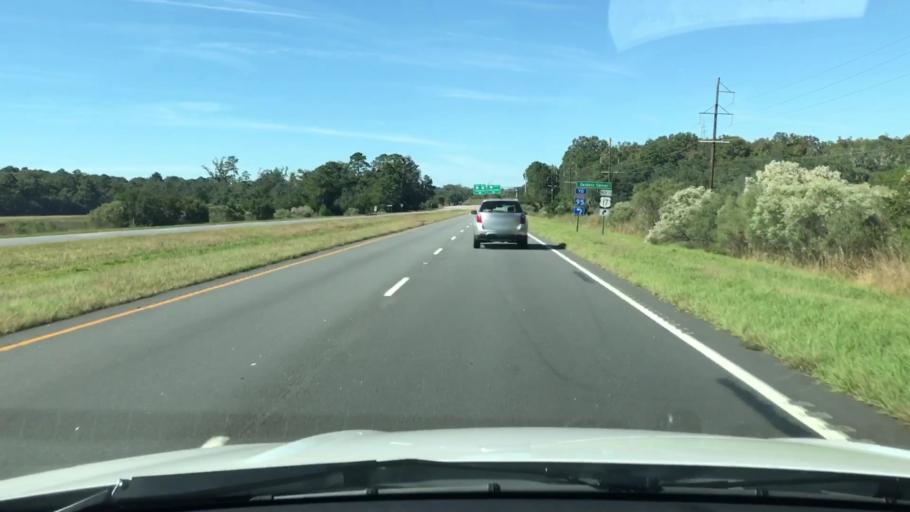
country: US
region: South Carolina
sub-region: Hampton County
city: Yemassee
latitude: 32.5965
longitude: -80.7547
